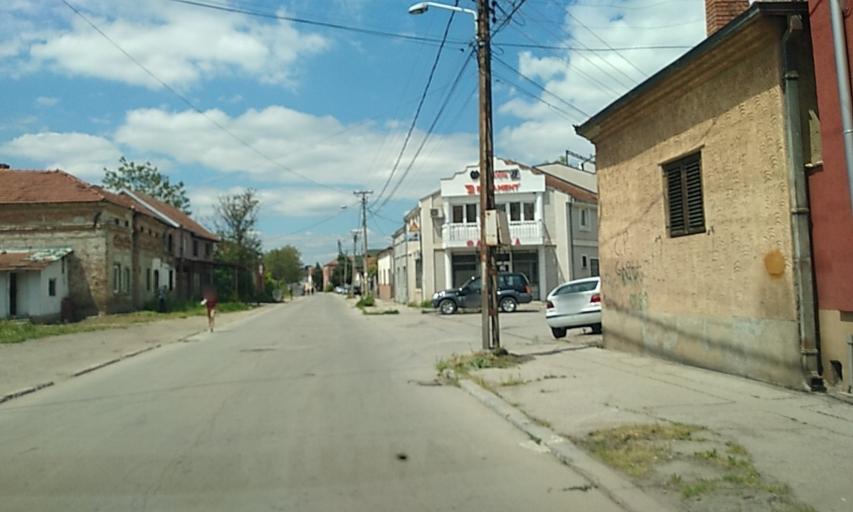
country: RS
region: Central Serbia
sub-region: Nisavski Okrug
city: Nis
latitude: 43.3201
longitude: 21.8854
